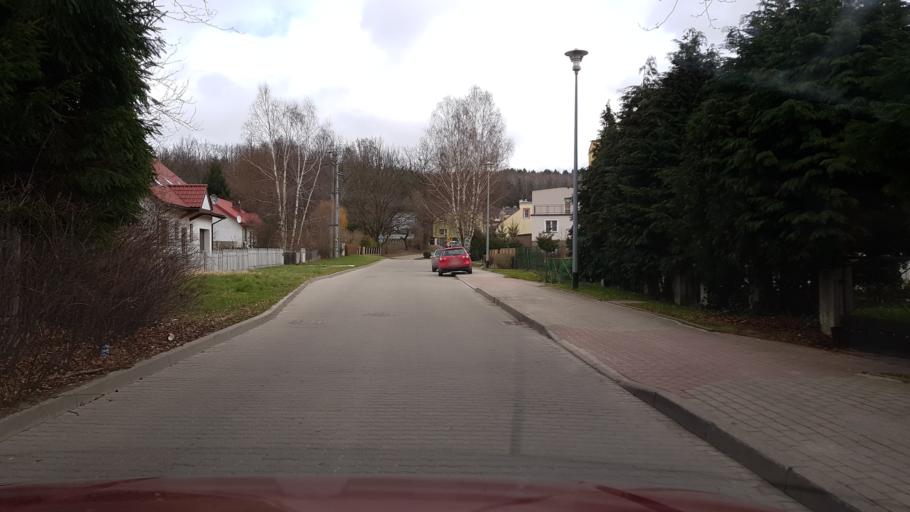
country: PL
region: West Pomeranian Voivodeship
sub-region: Powiat koszalinski
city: Sianow
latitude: 54.1899
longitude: 16.2379
